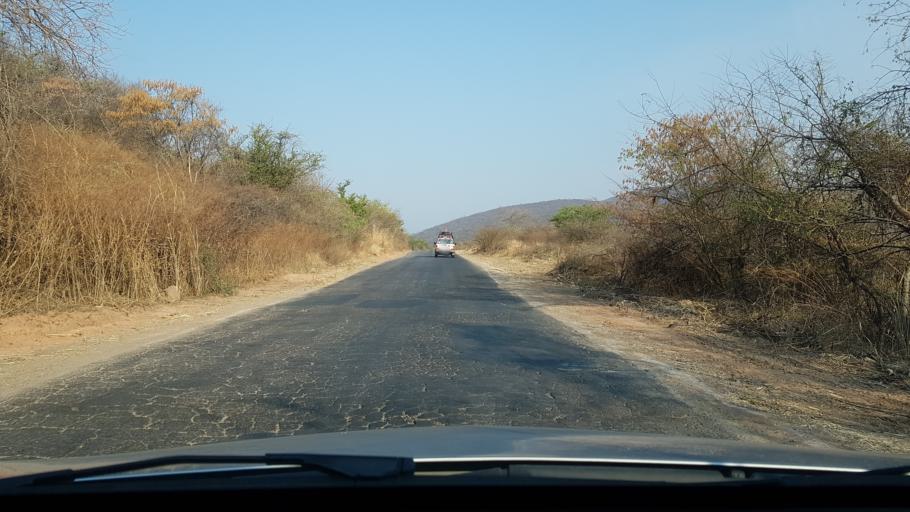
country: MX
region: Morelos
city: Tlaltizapan
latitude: 18.6714
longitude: -99.0559
